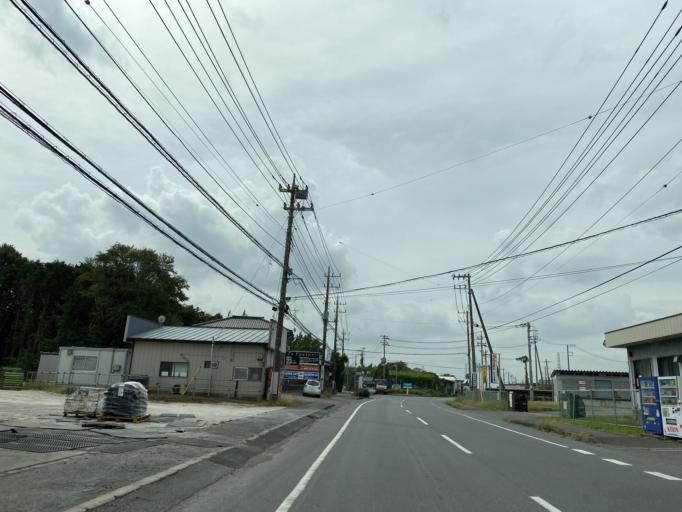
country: JP
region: Ibaraki
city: Mitsukaido
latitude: 36.0306
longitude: 140.0486
